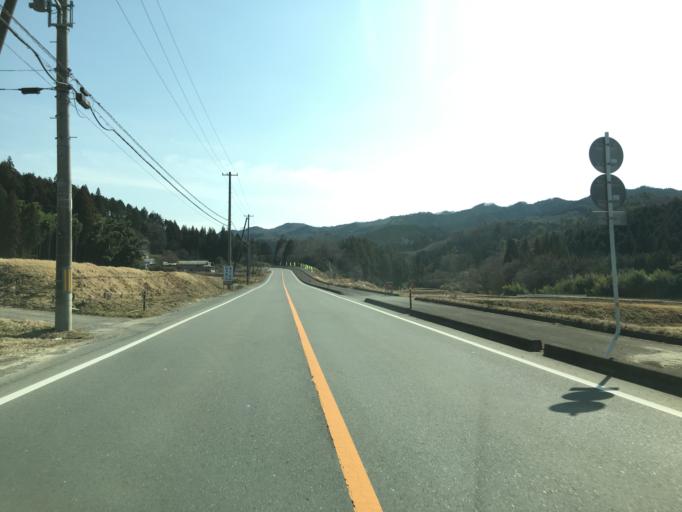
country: JP
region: Ibaraki
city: Daigo
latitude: 36.8238
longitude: 140.4585
